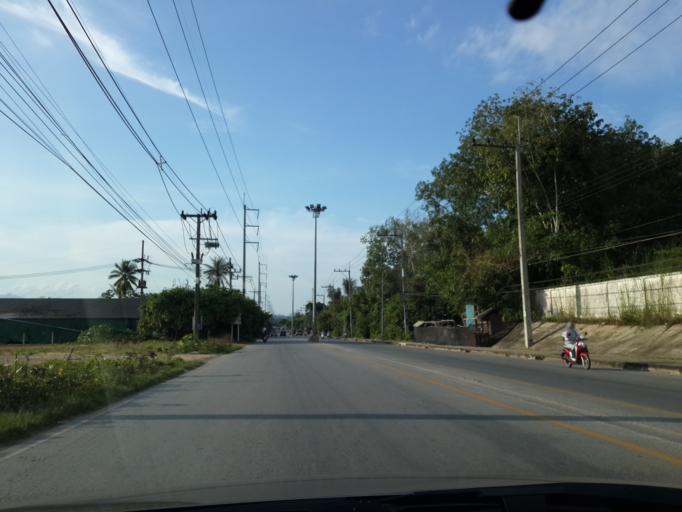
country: TH
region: Yala
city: Yala
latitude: 6.5180
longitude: 101.2691
